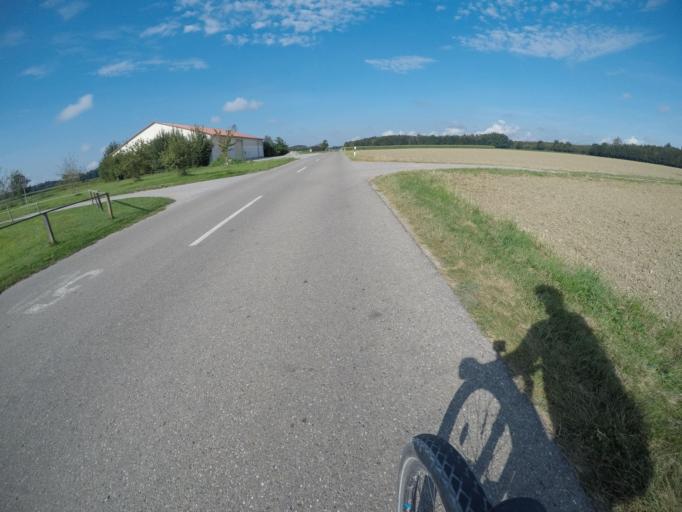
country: DE
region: Bavaria
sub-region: Swabia
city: Allmannshofen
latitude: 48.6140
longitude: 10.8013
